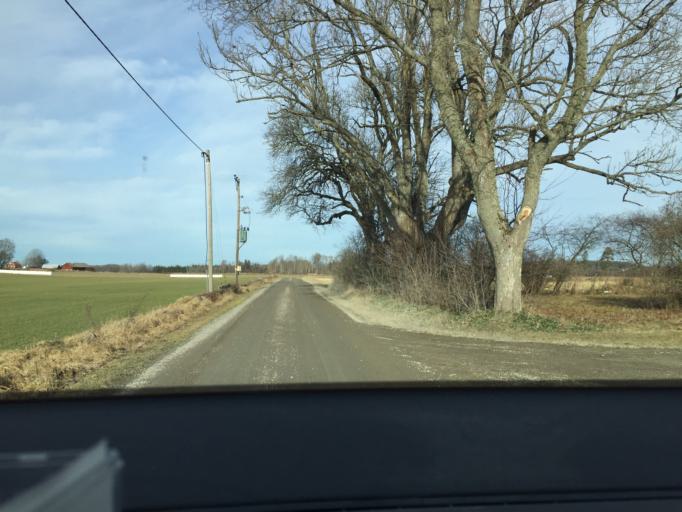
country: SE
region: OErebro
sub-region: Hallsbergs Kommun
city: Skollersta
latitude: 59.1334
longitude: 15.4288
